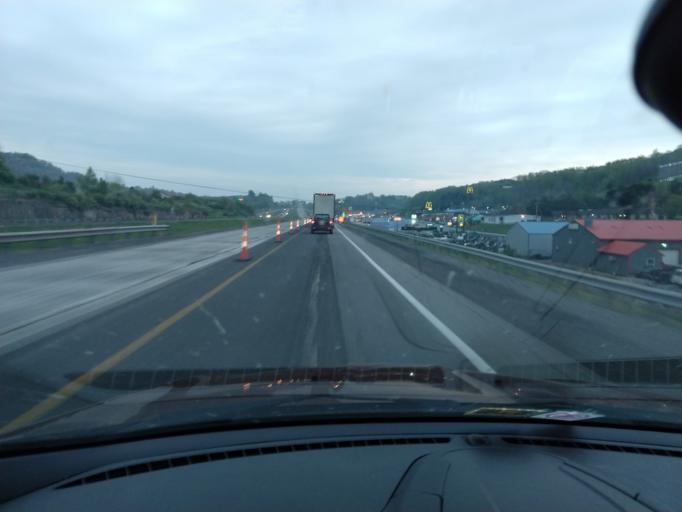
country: US
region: West Virginia
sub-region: Braxton County
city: Sutton
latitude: 38.6974
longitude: -80.6682
